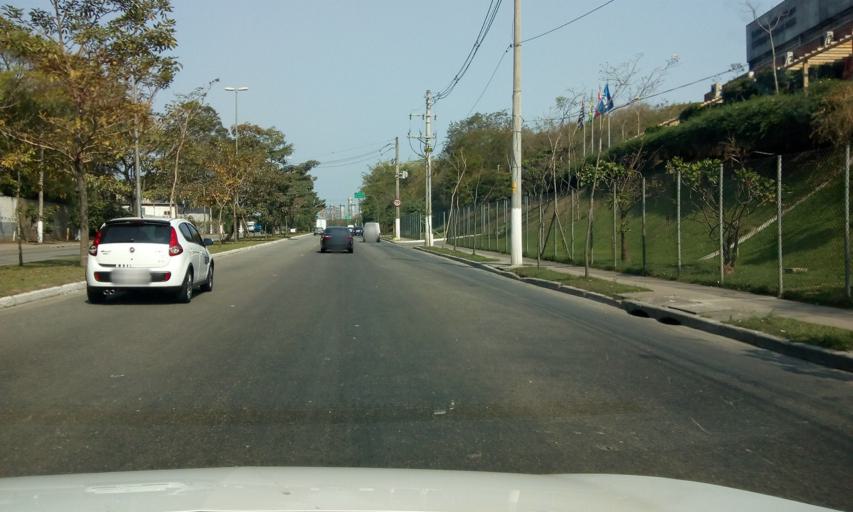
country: BR
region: Sao Paulo
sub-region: Diadema
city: Diadema
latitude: -23.6922
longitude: -46.6852
